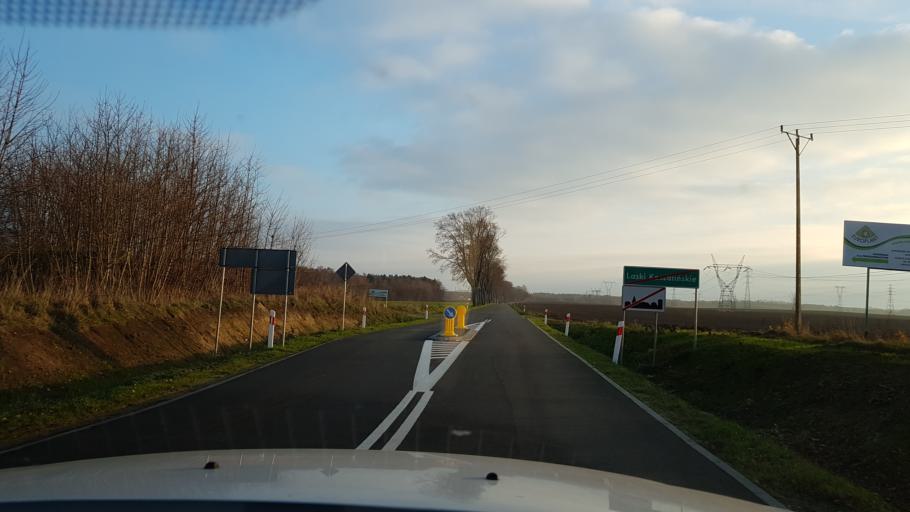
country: PL
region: West Pomeranian Voivodeship
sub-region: Koszalin
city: Koszalin
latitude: 54.1371
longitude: 16.0824
